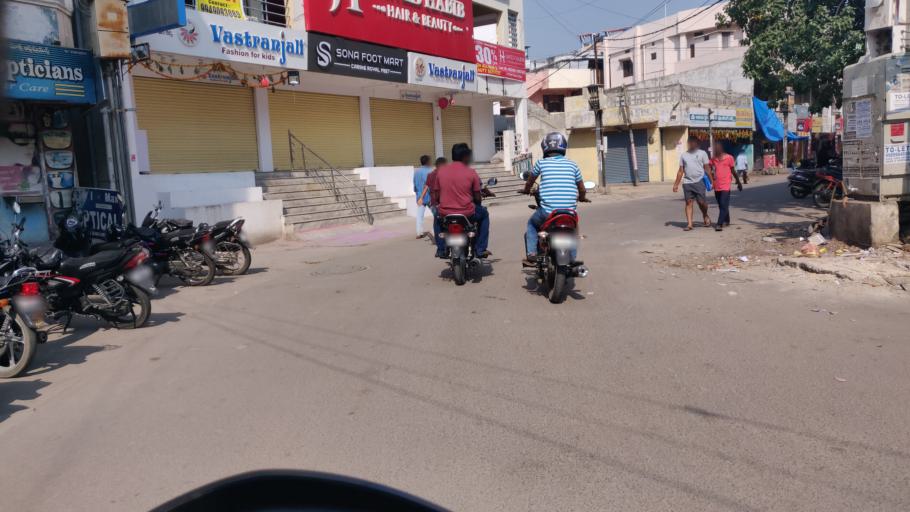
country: IN
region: Telangana
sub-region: Rangareddi
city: Gaddi Annaram
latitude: 17.3645
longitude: 78.5259
